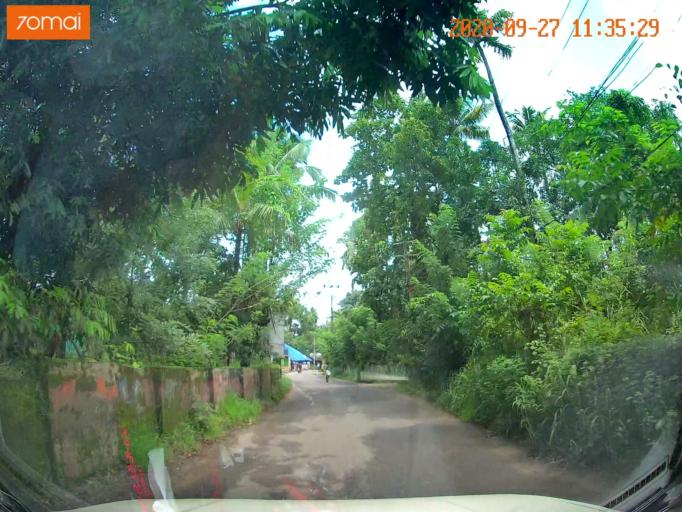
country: IN
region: Kerala
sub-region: Thrissur District
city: Thanniyam
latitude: 10.4438
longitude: 76.1256
